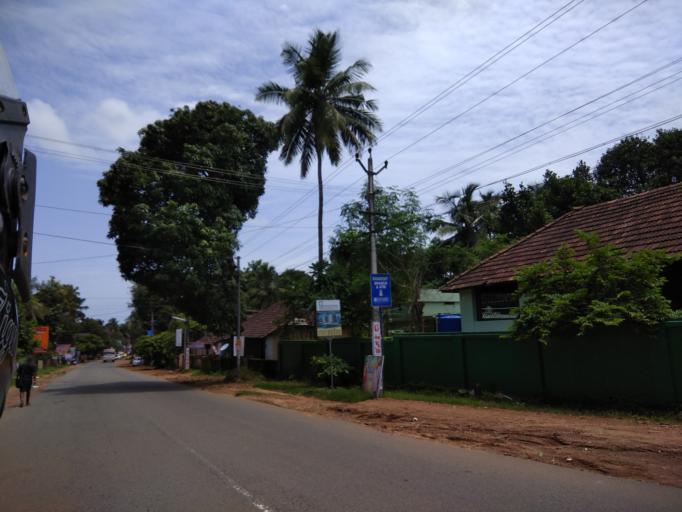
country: IN
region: Kerala
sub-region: Thrissur District
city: Trichur
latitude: 10.4975
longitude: 76.1572
